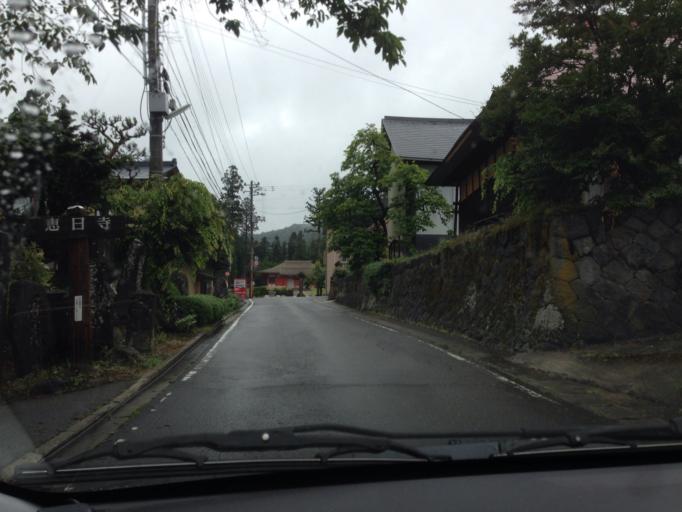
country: JP
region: Fukushima
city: Inawashiro
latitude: 37.5670
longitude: 139.9877
